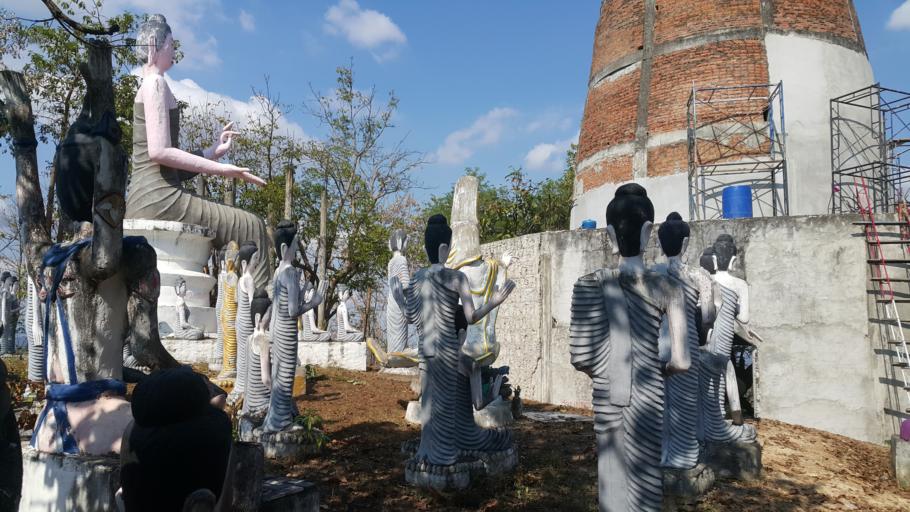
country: TH
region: Sukhothai
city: Thung Saliam
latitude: 17.3421
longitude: 99.5864
